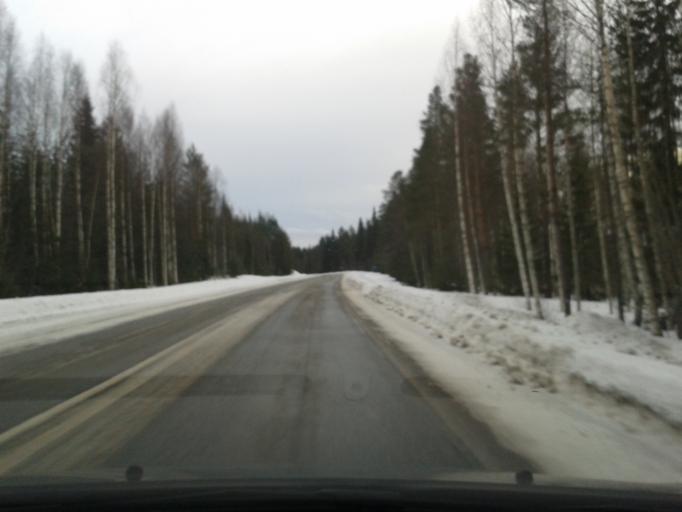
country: SE
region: Vaesternorrland
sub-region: Solleftea Kommun
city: As
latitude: 63.6584
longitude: 16.7873
